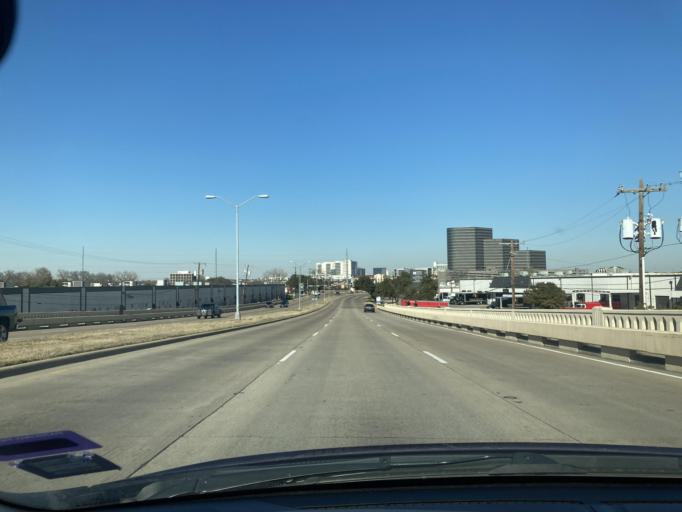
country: US
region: Texas
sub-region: Dallas County
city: Dallas
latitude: 32.8034
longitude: -96.8532
